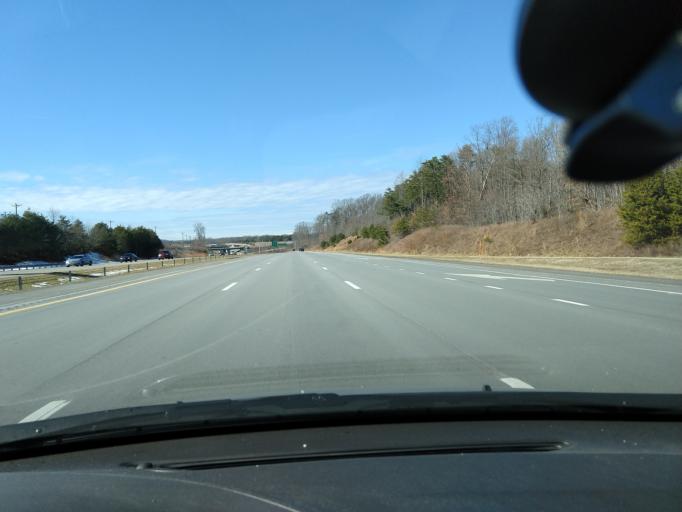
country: US
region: North Carolina
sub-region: Guilford County
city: Oak Ridge
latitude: 36.1204
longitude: -79.9189
